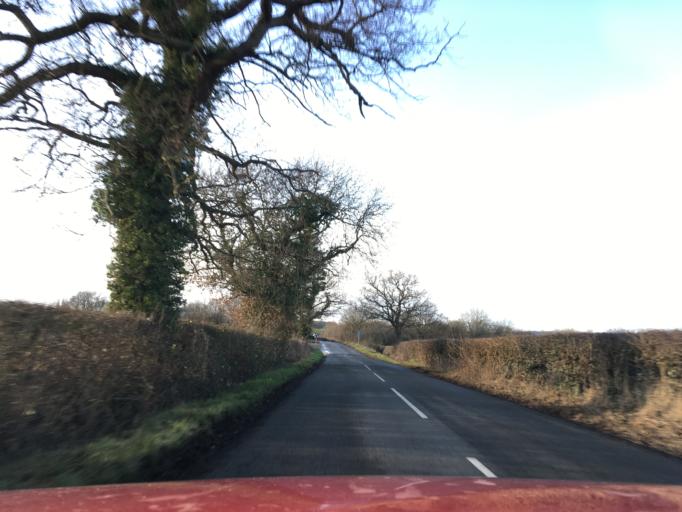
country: GB
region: England
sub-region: Warwickshire
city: Henley in Arden
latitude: 52.2464
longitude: -1.7896
